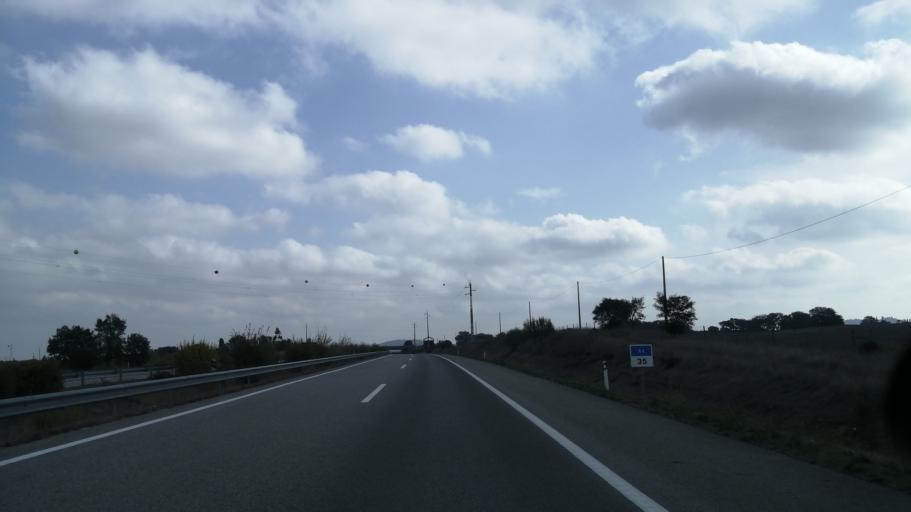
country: PT
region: Evora
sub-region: Montemor-O-Novo
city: Montemor-o-Novo
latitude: 38.6455
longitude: -8.2621
